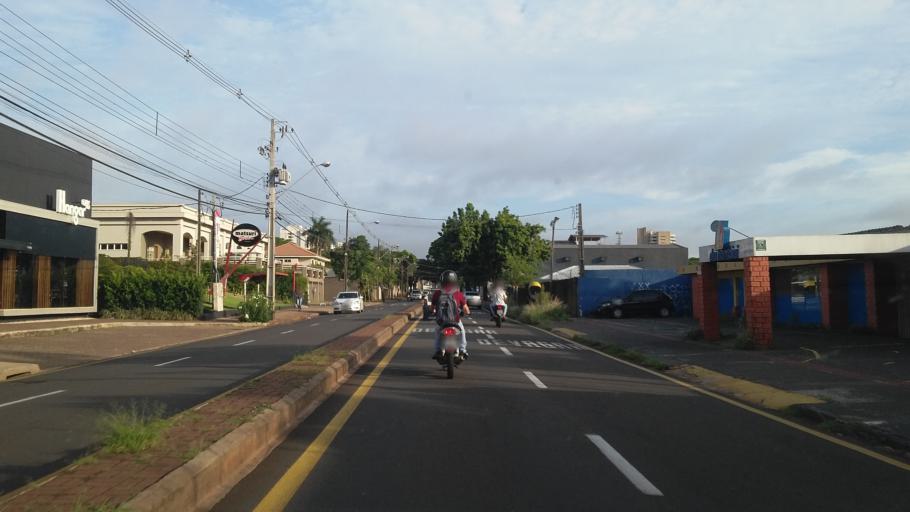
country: BR
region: Parana
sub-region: Londrina
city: Londrina
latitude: -23.3178
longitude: -51.1769
